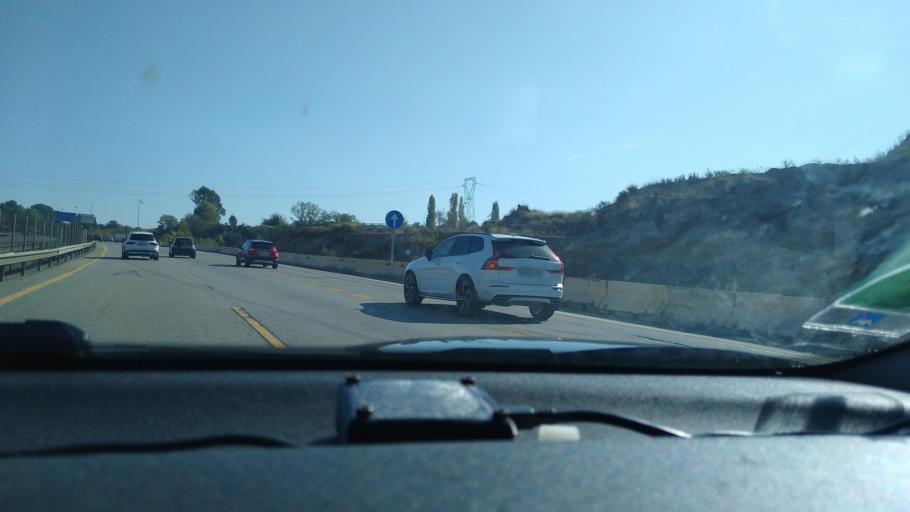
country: ES
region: Catalonia
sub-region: Provincia de Barcelona
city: Viladecavalls
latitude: 41.5548
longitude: 1.9797
